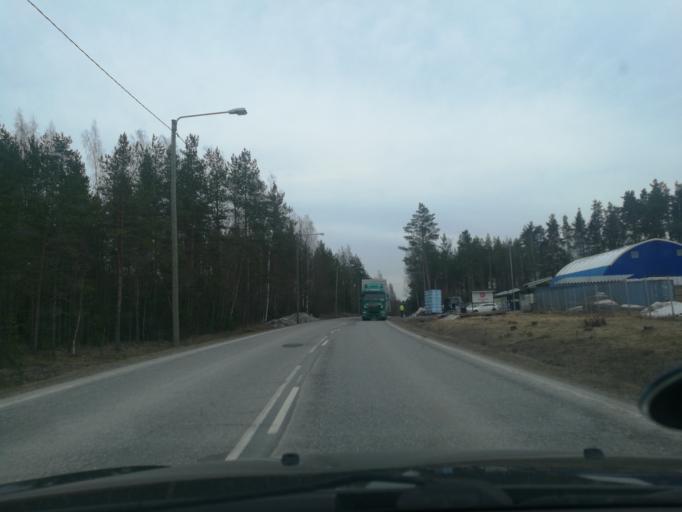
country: FI
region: Uusimaa
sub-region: Helsinki
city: Nickby
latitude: 60.2933
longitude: 25.3635
